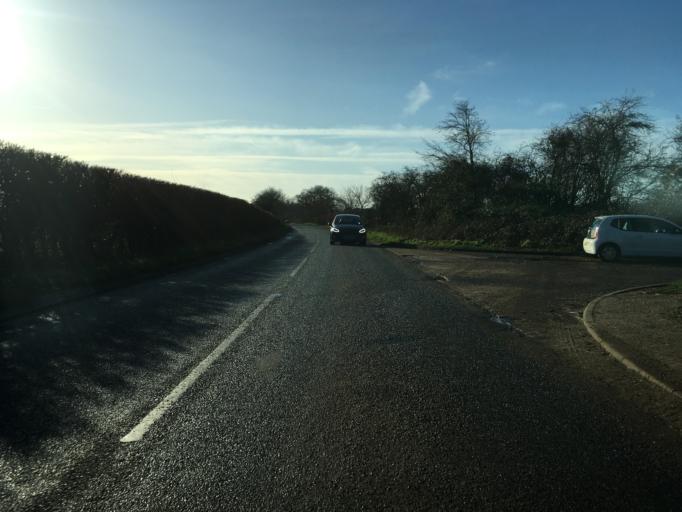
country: GB
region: England
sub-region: Warwickshire
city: Wellesbourne Mountford
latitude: 52.2156
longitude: -1.6083
